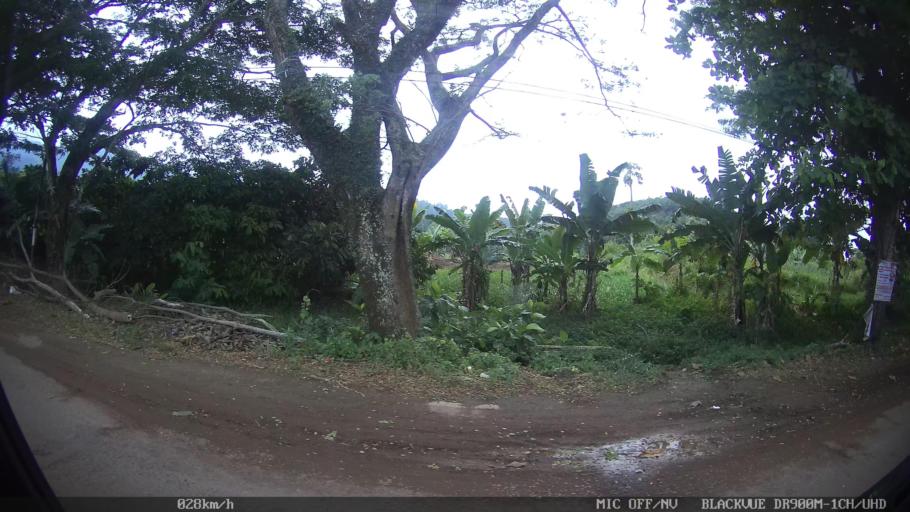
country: ID
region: Lampung
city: Bandarlampung
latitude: -5.4136
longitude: 105.1915
